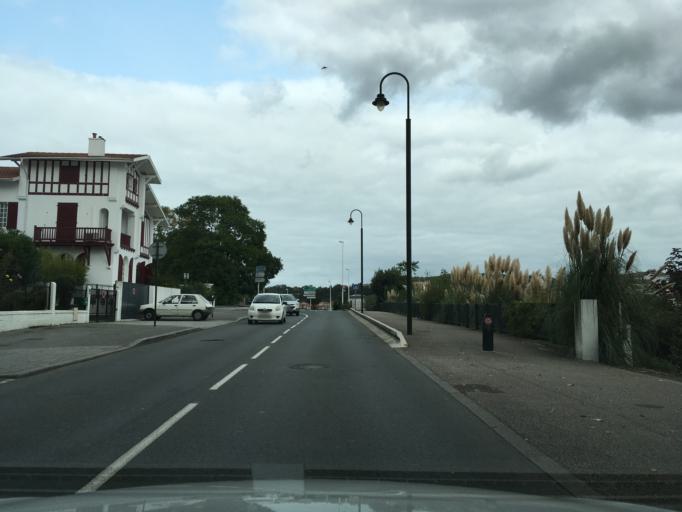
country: FR
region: Aquitaine
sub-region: Departement des Pyrenees-Atlantiques
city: Bayonne
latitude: 43.4898
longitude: -1.4670
